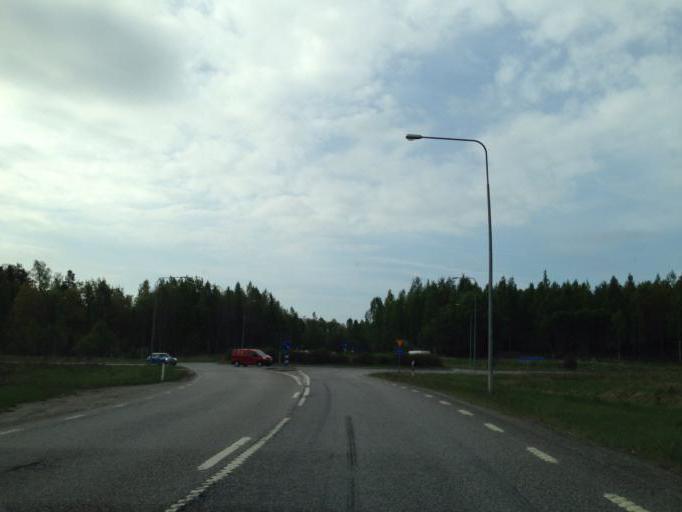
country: SE
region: Soedermanland
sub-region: Eskilstuna Kommun
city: Skogstorp
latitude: 59.3317
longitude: 16.4635
